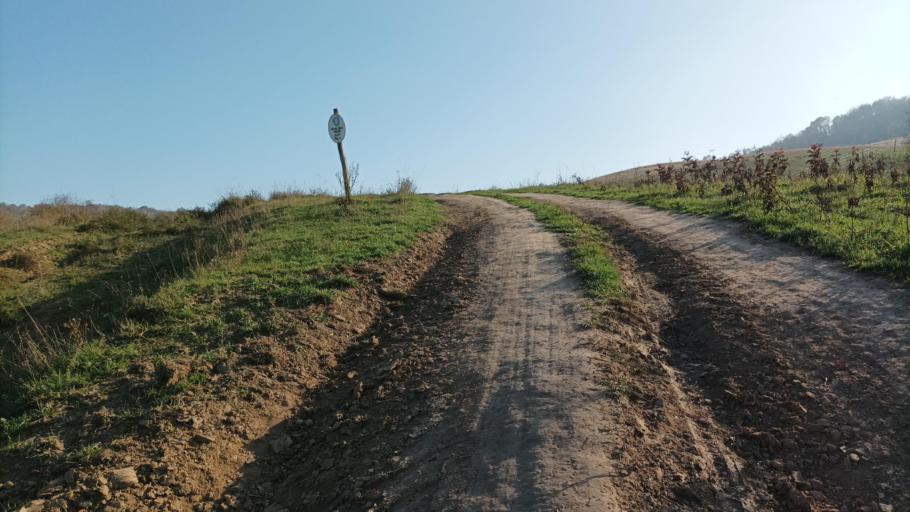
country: HU
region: Tolna
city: Szentgalpuszta
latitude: 46.3390
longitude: 18.6038
